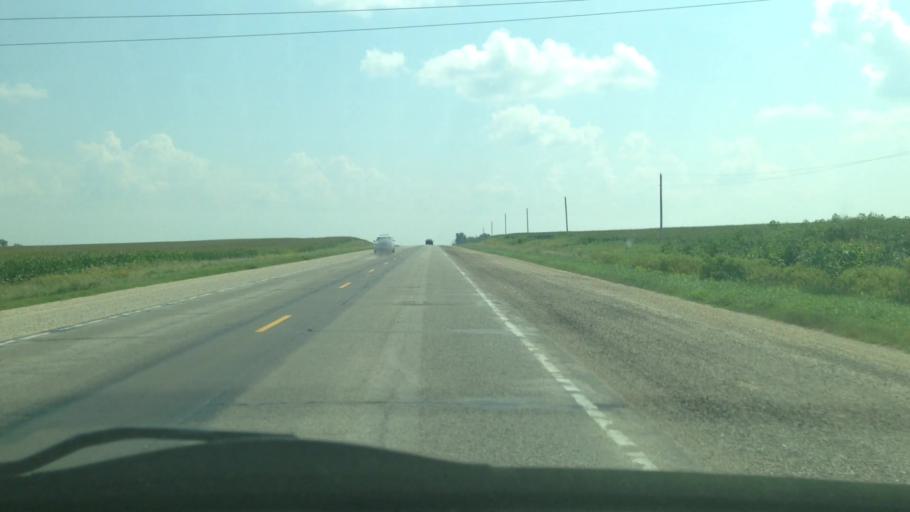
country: US
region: Iowa
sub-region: Howard County
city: Cresco
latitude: 43.3640
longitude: -92.2985
